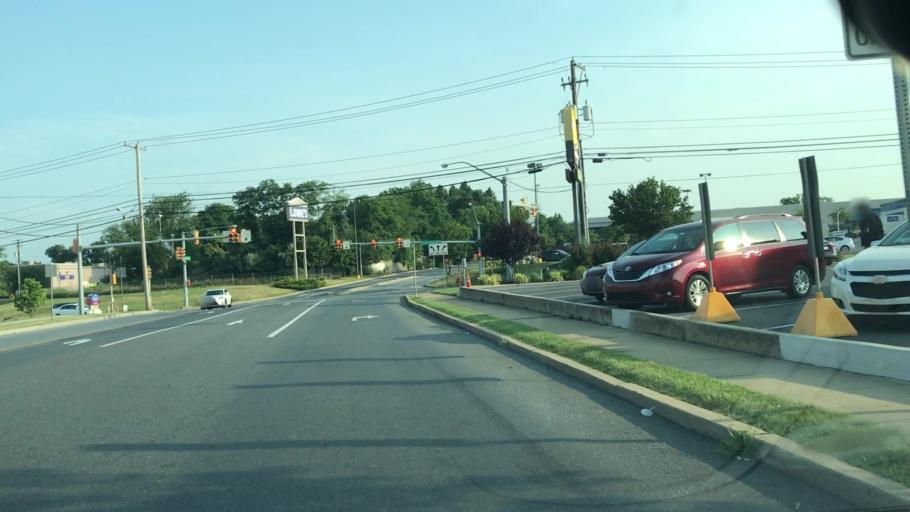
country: US
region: Pennsylvania
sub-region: Dauphin County
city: Progress
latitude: 40.2777
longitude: -76.8220
